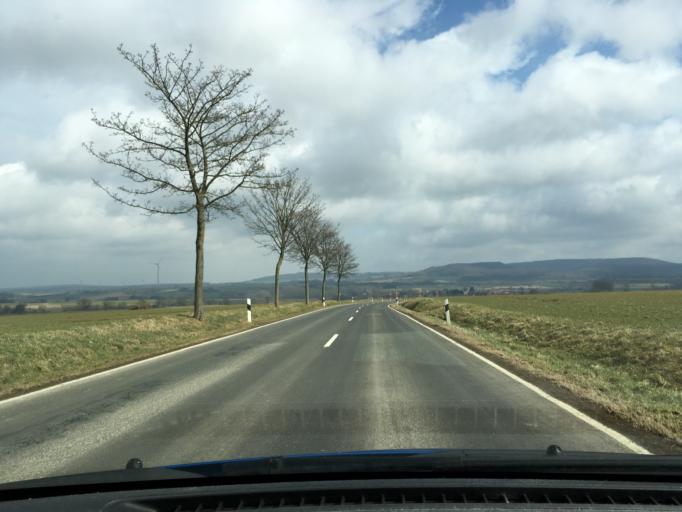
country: DE
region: Lower Saxony
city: Buhren
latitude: 51.5088
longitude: 9.6880
